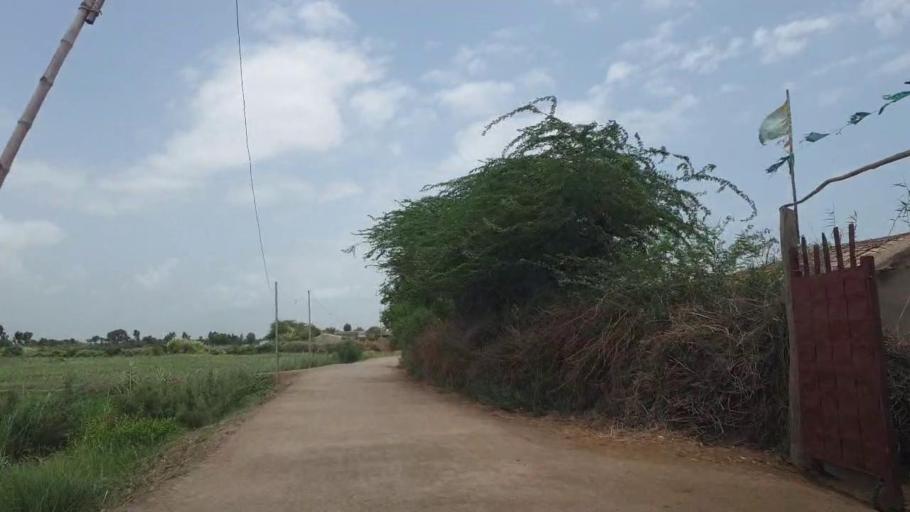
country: PK
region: Sindh
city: Badin
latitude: 24.6615
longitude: 68.9038
